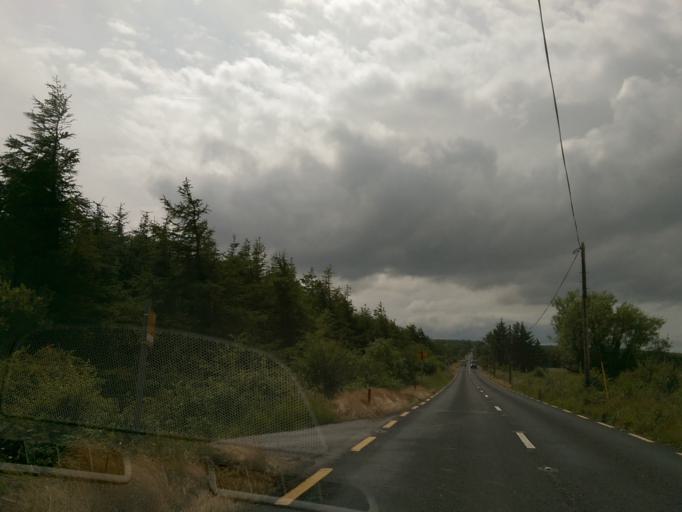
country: IE
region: Munster
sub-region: An Clar
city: Kilrush
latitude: 52.6876
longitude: -9.3569
